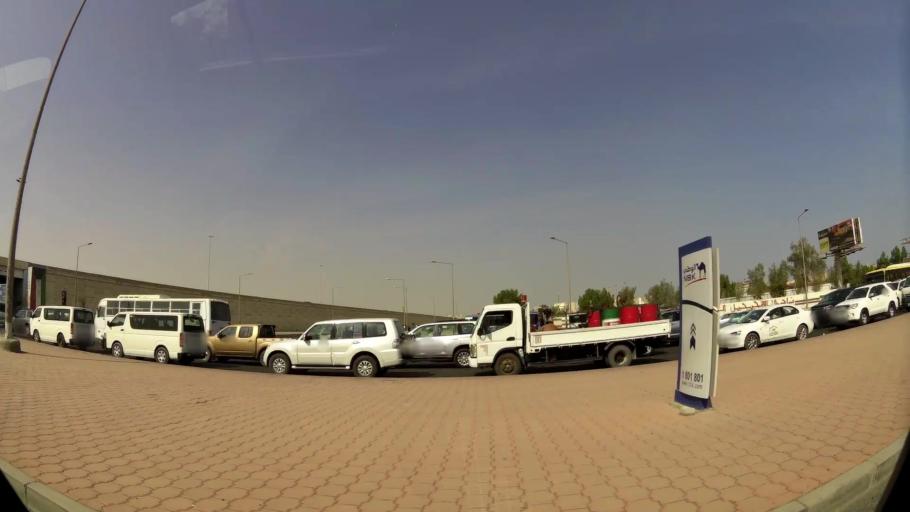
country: KW
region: Al Ahmadi
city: Al Fahahil
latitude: 29.0907
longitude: 48.1169
